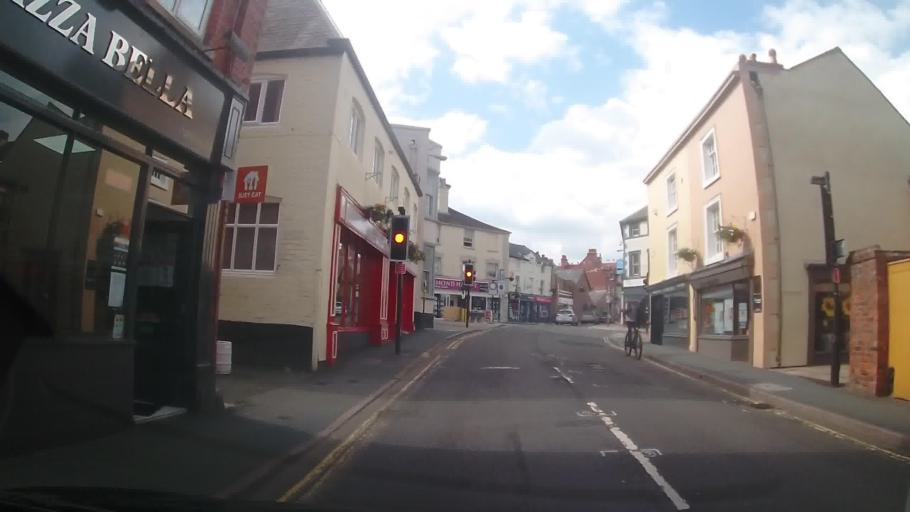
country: GB
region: England
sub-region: Shropshire
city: Oswestry
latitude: 52.8595
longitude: -3.0534
